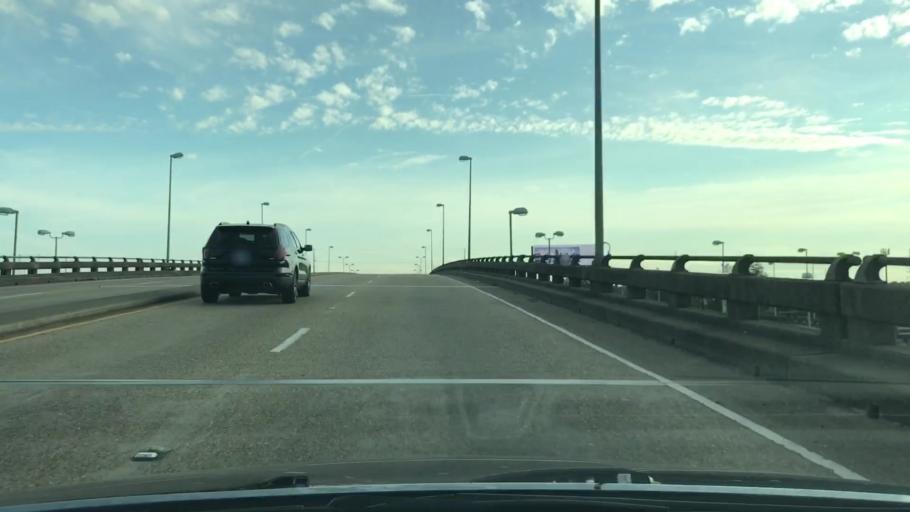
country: US
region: Louisiana
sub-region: Jefferson Parish
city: Metairie Terrace
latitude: 29.9761
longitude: -90.1564
